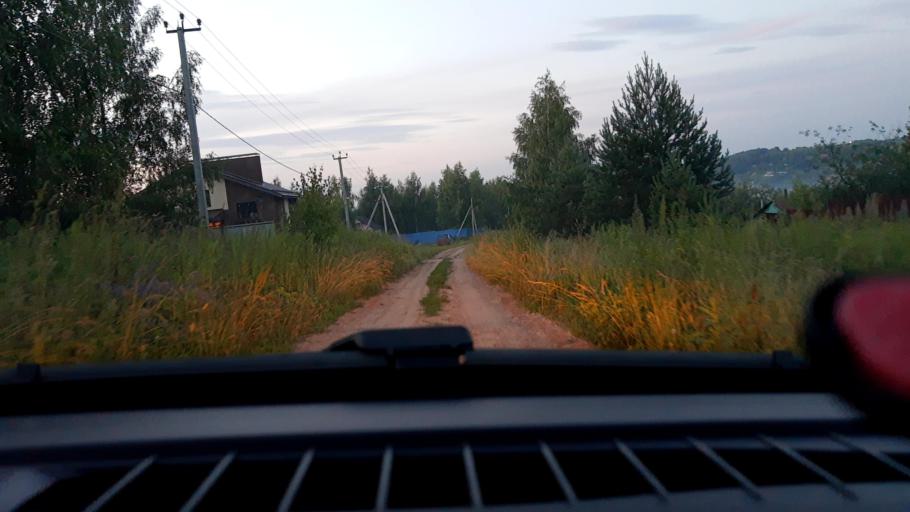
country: RU
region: Nizjnij Novgorod
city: Afonino
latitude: 56.2514
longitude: 44.0662
